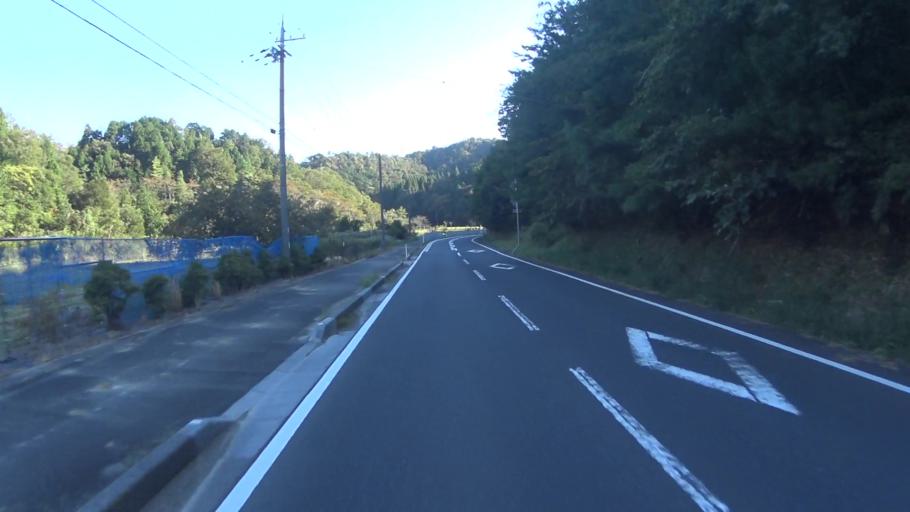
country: JP
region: Hyogo
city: Toyooka
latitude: 35.6255
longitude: 134.8881
